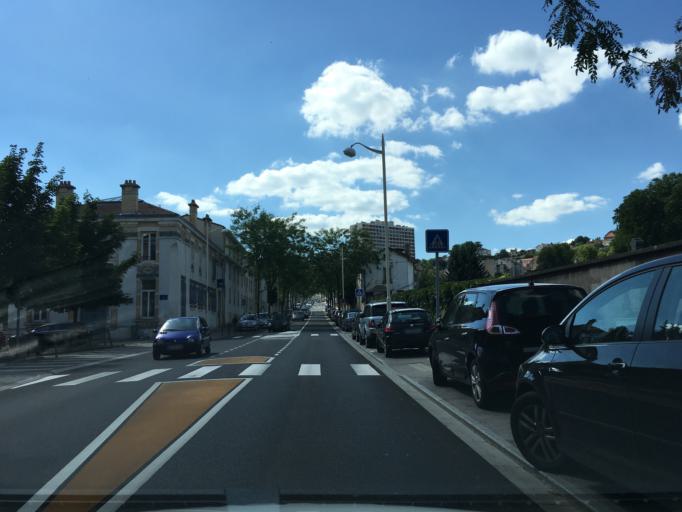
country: FR
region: Lorraine
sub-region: Departement de Meurthe-et-Moselle
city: Laxou
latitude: 48.6887
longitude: 6.1642
